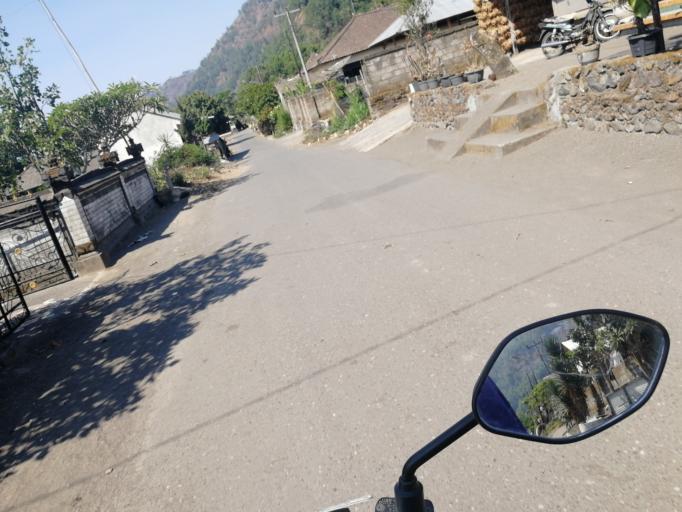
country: ID
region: Bali
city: Banjar Trunyan
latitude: -8.2751
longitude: 115.4138
